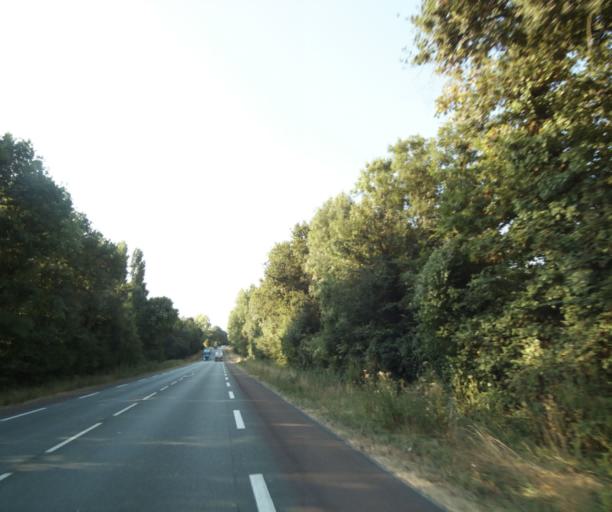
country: FR
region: Poitou-Charentes
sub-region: Departement de la Charente-Maritime
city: Cabariot
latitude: 45.9422
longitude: -0.8643
